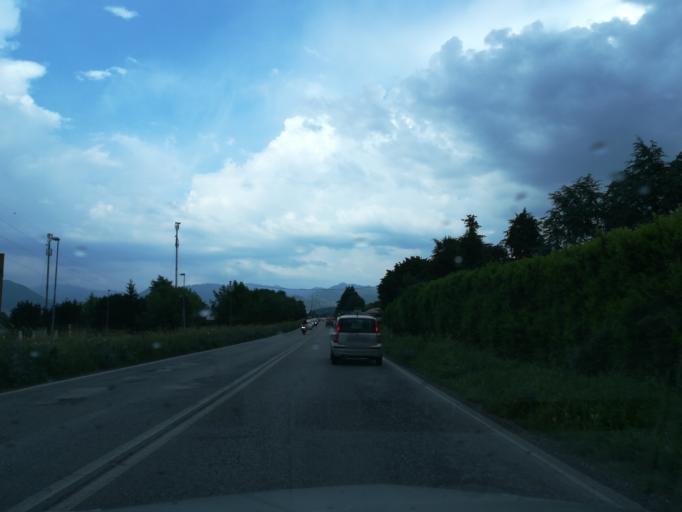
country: IT
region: Lombardy
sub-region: Provincia di Bergamo
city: Mozzo
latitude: 45.6987
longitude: 9.6038
